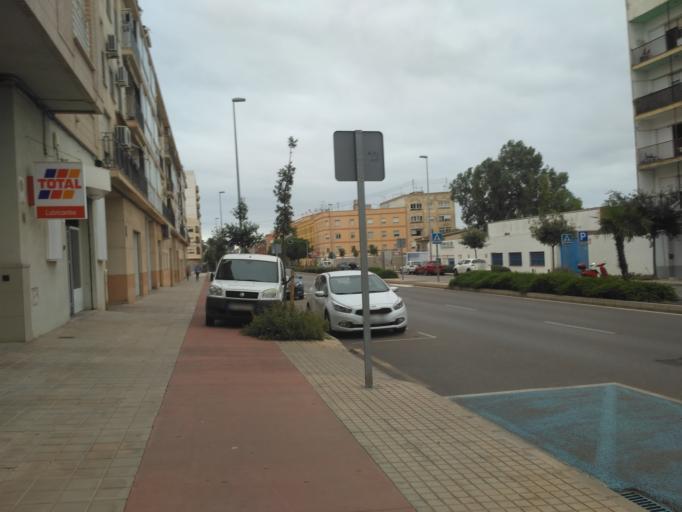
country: ES
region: Valencia
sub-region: Provincia de Castello
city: Castello de la Plana
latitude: 39.9881
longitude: -0.0645
